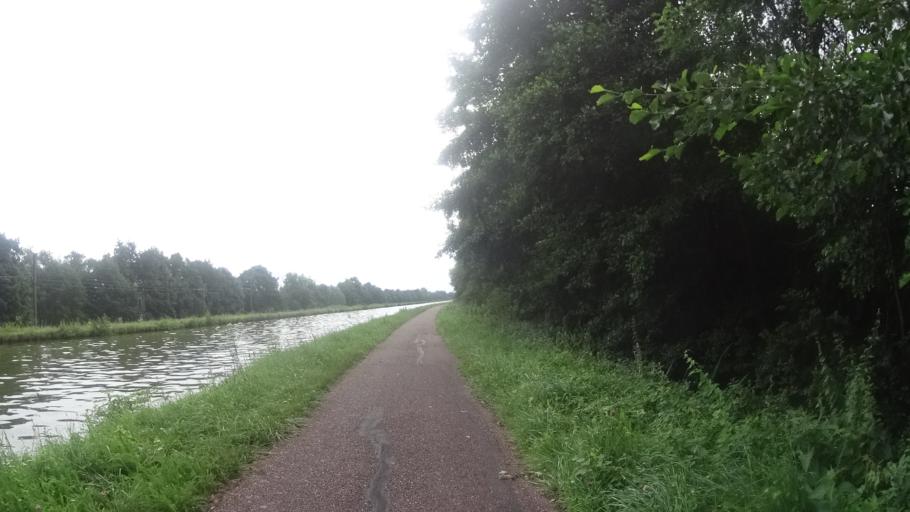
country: FR
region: Alsace
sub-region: Departement du Bas-Rhin
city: Steinbourg
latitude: 48.7623
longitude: 7.4354
